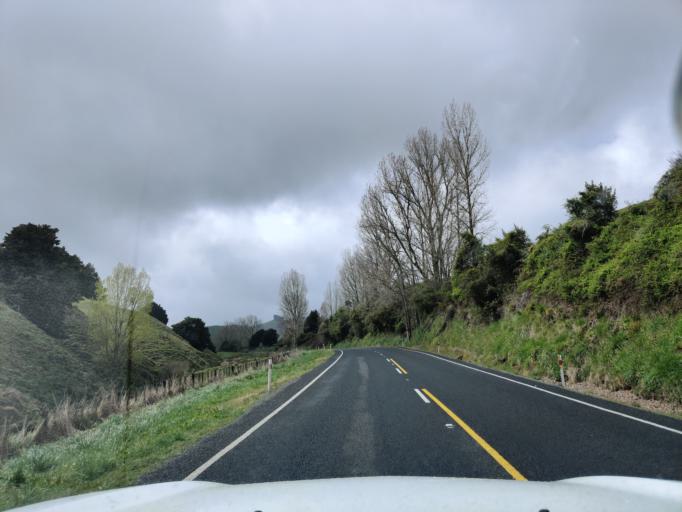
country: NZ
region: Waikato
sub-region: Otorohanga District
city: Otorohanga
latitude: -38.6984
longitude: 175.2337
